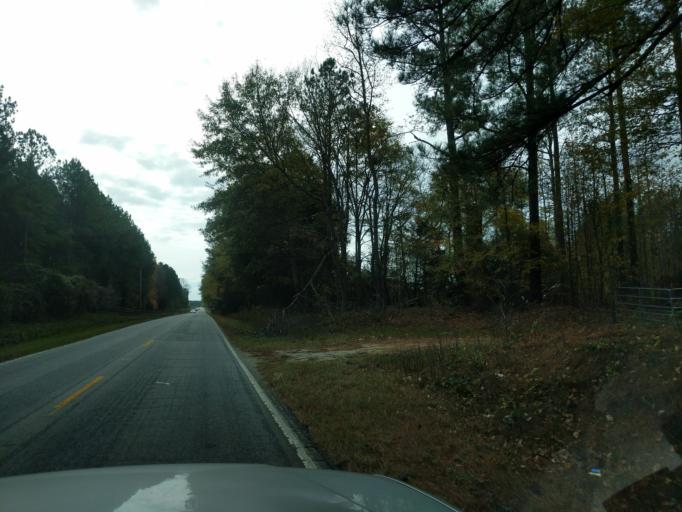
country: US
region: South Carolina
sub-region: Laurens County
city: Joanna
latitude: 34.3709
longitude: -81.8601
